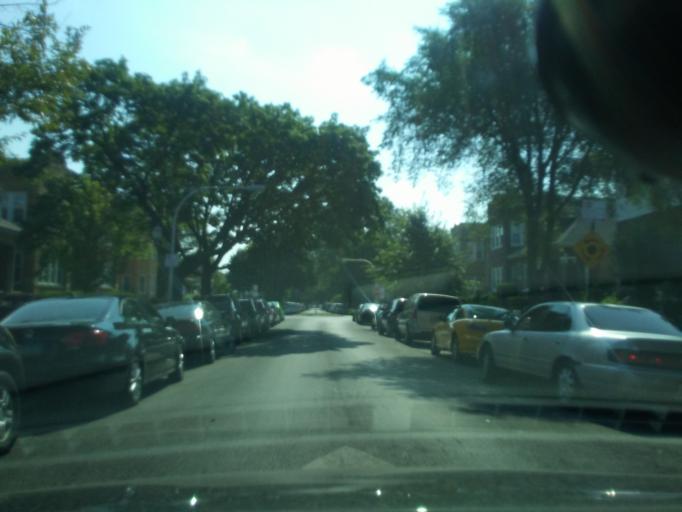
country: US
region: Illinois
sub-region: Cook County
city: Elmwood Park
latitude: 41.9369
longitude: -87.7550
